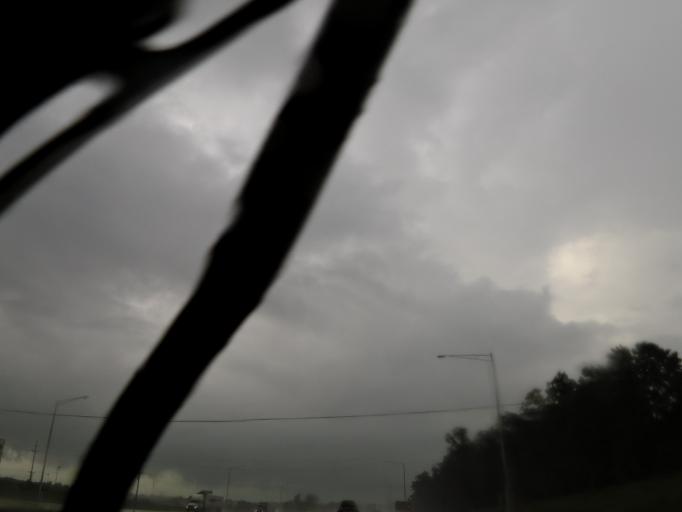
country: US
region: Illinois
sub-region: Jefferson County
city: Mount Vernon
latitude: 38.3176
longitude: -88.9538
